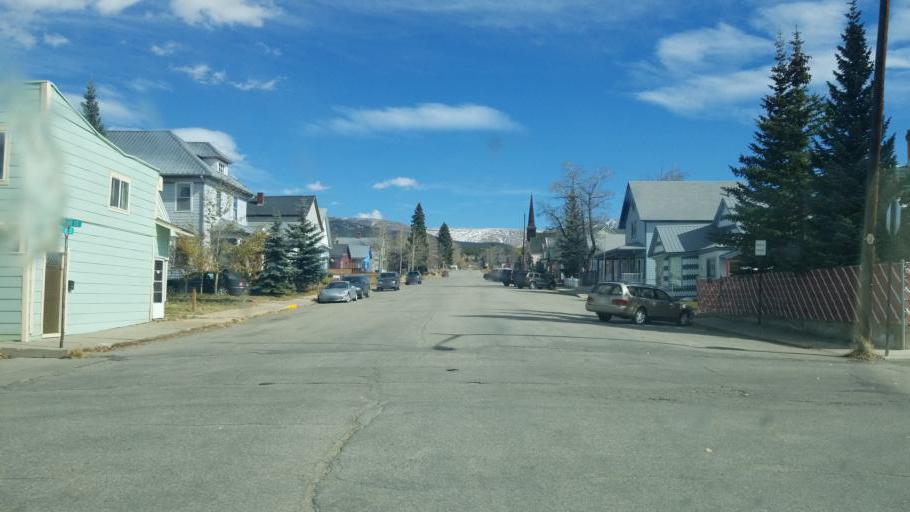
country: US
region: Colorado
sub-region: Lake County
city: Leadville
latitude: 39.2508
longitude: -106.2905
